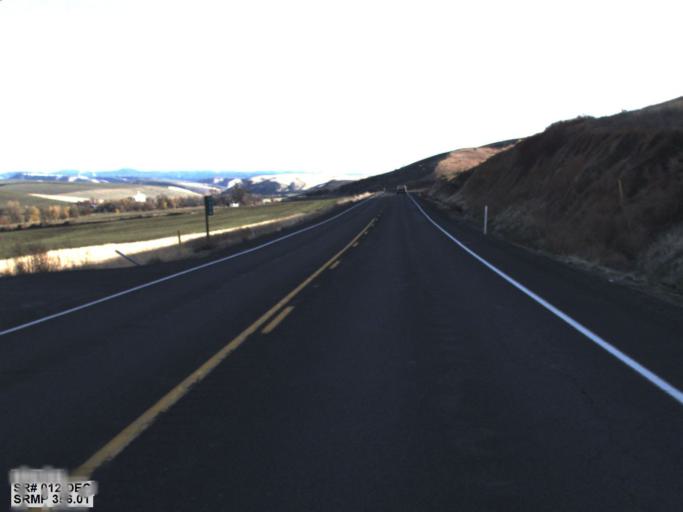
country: US
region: Washington
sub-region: Walla Walla County
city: Waitsburg
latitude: 46.2484
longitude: -118.1465
